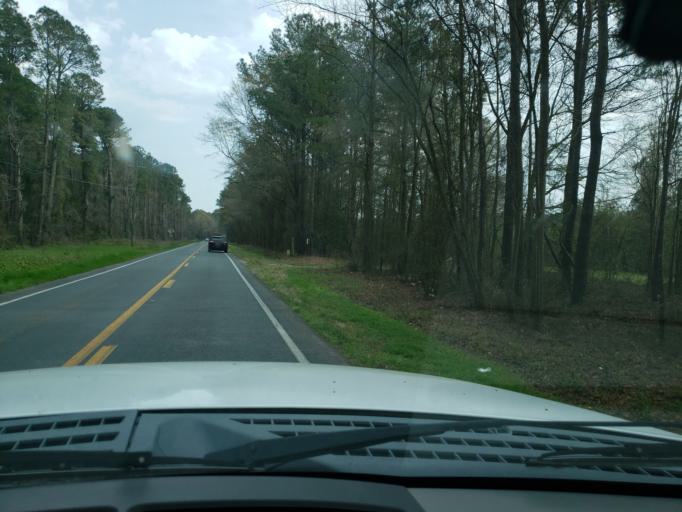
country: US
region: North Carolina
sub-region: Duplin County
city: Beulaville
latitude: 34.7895
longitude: -77.8437
